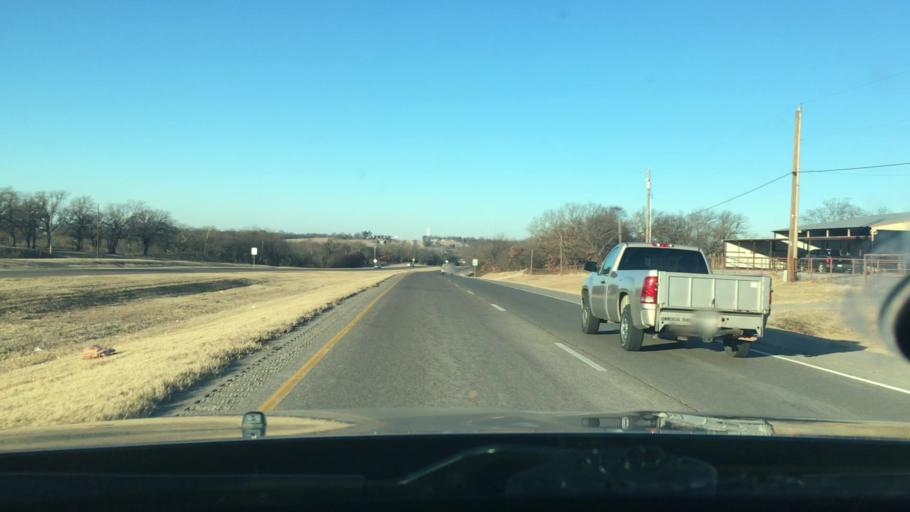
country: US
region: Oklahoma
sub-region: Murray County
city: Sulphur
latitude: 34.5064
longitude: -97.0205
